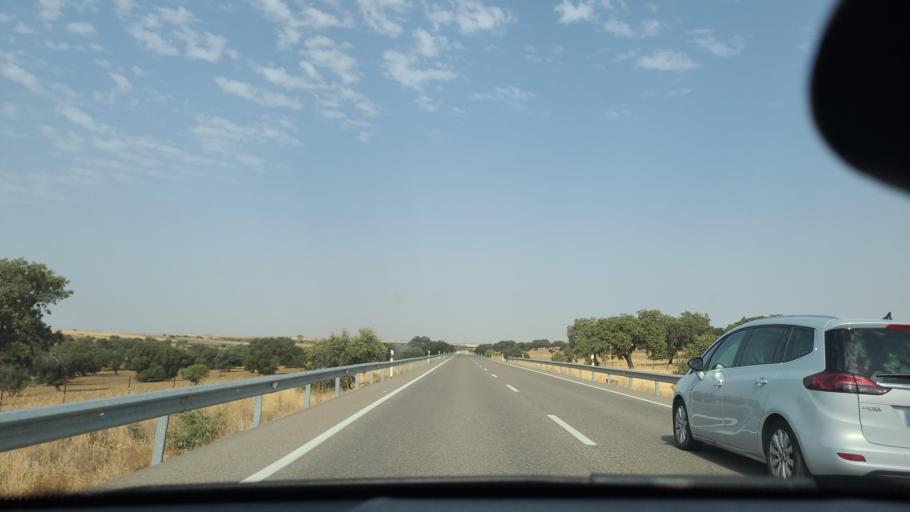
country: ES
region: Andalusia
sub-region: Province of Cordoba
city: Fuente Obejuna
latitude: 38.2625
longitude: -5.4878
